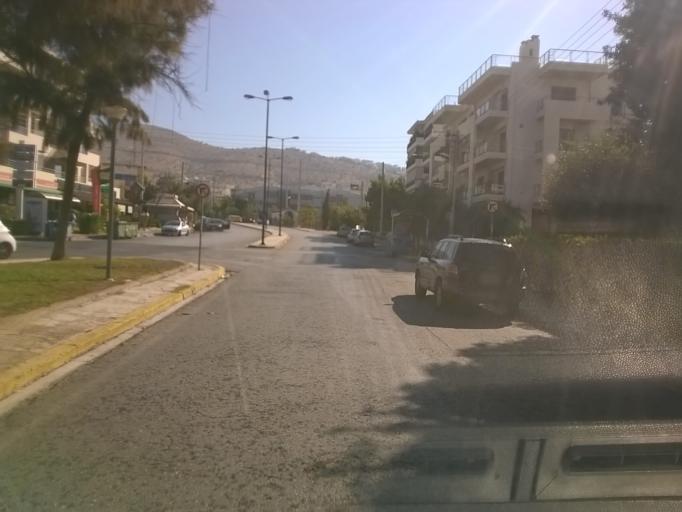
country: GR
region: Attica
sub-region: Nomarchia Athinas
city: Glyfada
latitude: 37.8607
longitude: 23.7615
